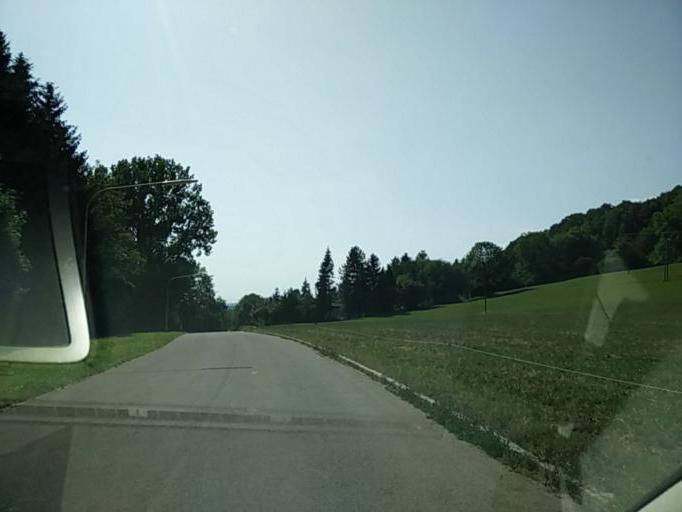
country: DE
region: Baden-Wuerttemberg
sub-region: Tuebingen Region
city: Gomaringen
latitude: 48.4130
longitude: 9.1279
